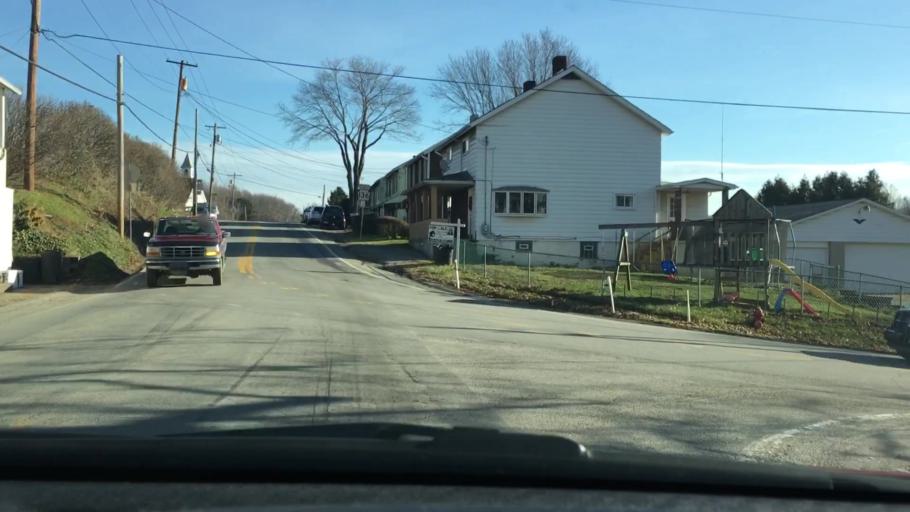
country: US
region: Pennsylvania
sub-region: Westmoreland County
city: Irwin
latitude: 40.2664
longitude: -79.6791
